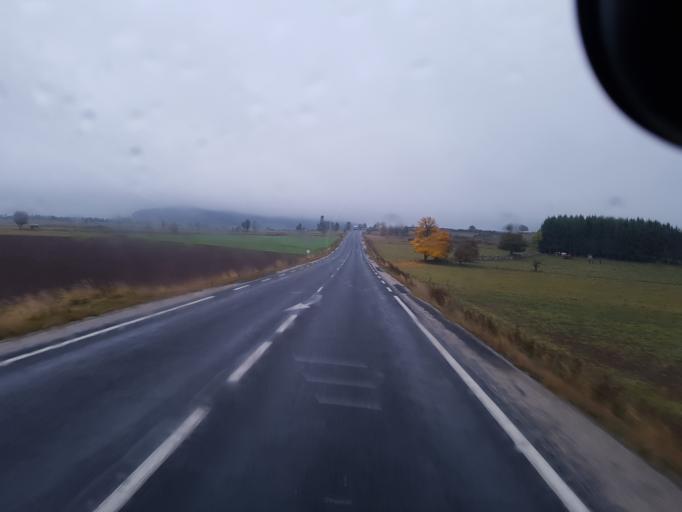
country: FR
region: Languedoc-Roussillon
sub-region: Departement de la Lozere
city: Langogne
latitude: 44.8455
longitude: 3.8555
